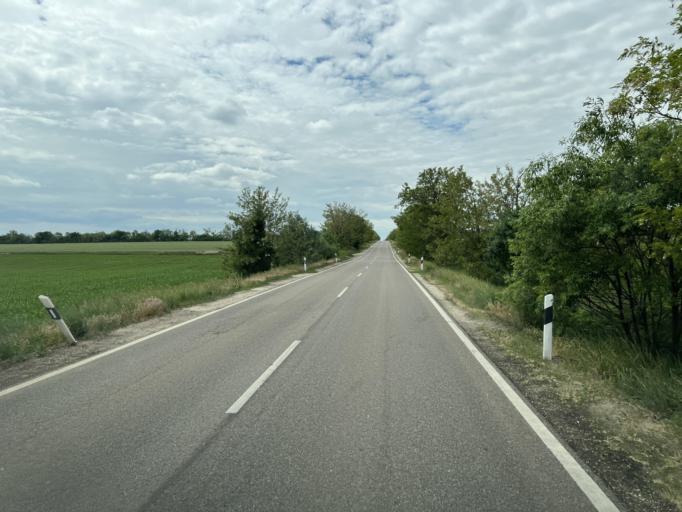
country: HU
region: Pest
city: Zsambok
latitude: 47.5329
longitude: 19.6035
